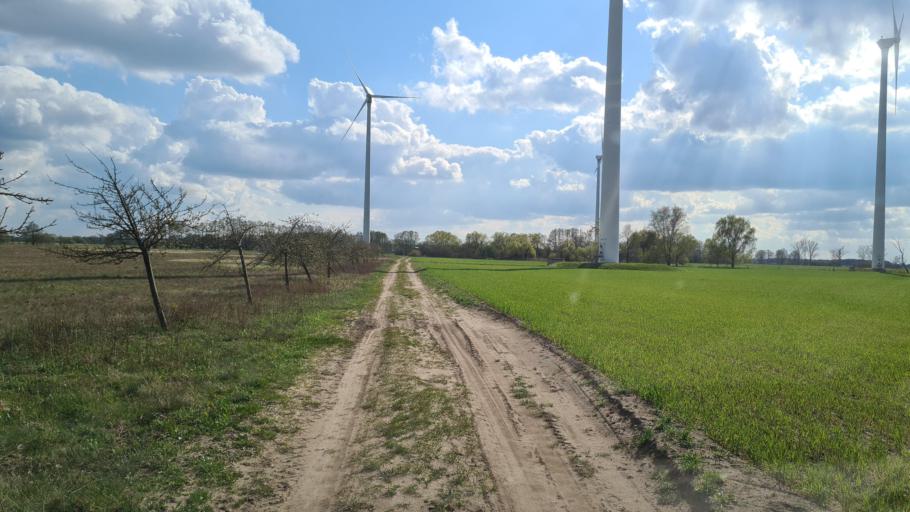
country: DE
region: Saxony-Anhalt
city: Holzdorf
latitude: 51.8282
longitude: 13.1529
